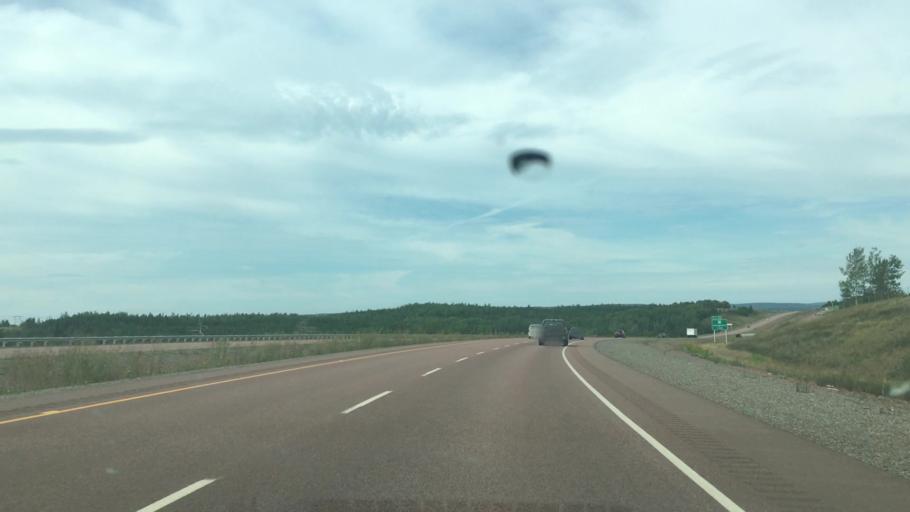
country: CA
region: Nova Scotia
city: Antigonish
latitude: 45.6004
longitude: -61.9465
